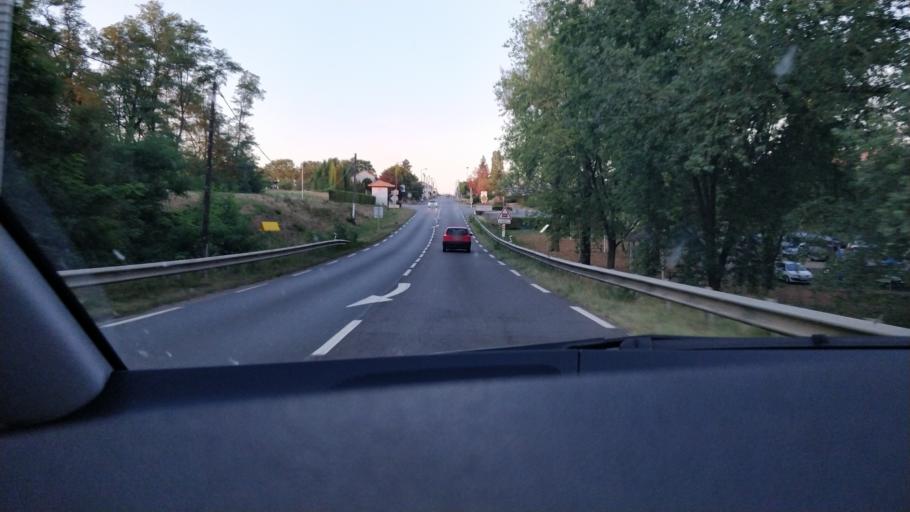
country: FR
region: Poitou-Charentes
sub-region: Departement de la Charente
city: Loubert
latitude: 45.8820
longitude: 0.5711
